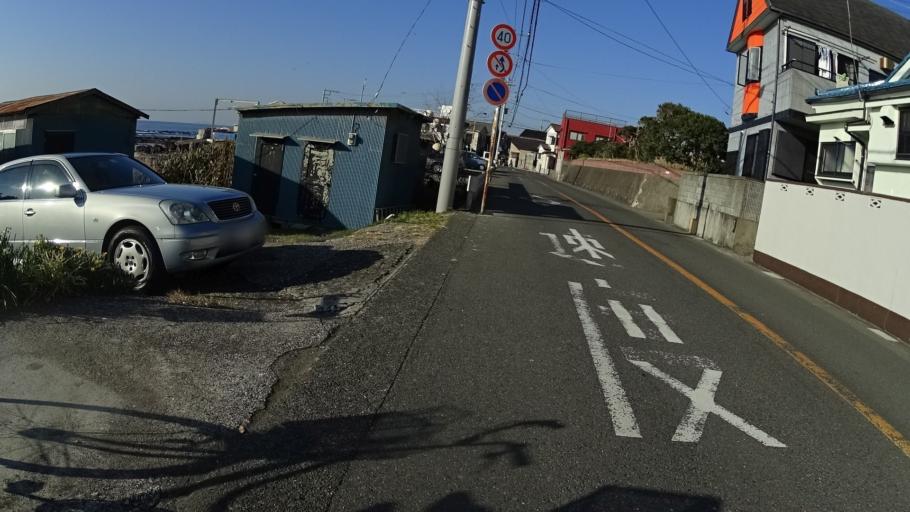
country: JP
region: Kanagawa
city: Miura
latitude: 35.2017
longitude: 139.6053
